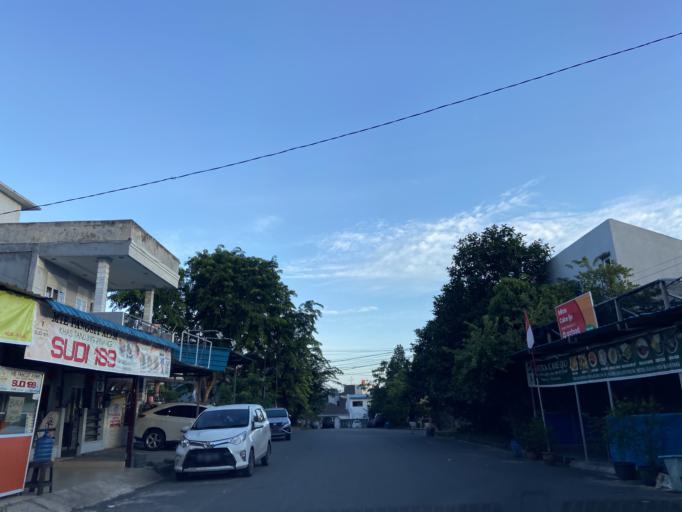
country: SG
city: Singapore
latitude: 1.1213
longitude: 104.0430
